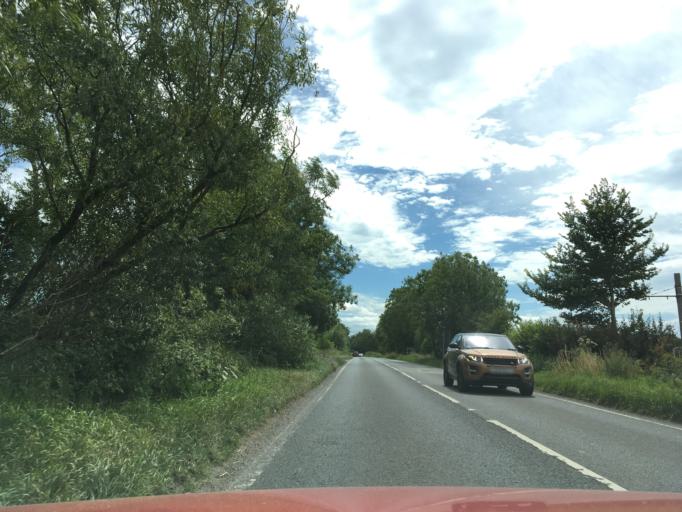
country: GB
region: England
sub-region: Somerset
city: Glastonbury
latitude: 51.1749
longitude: -2.6940
